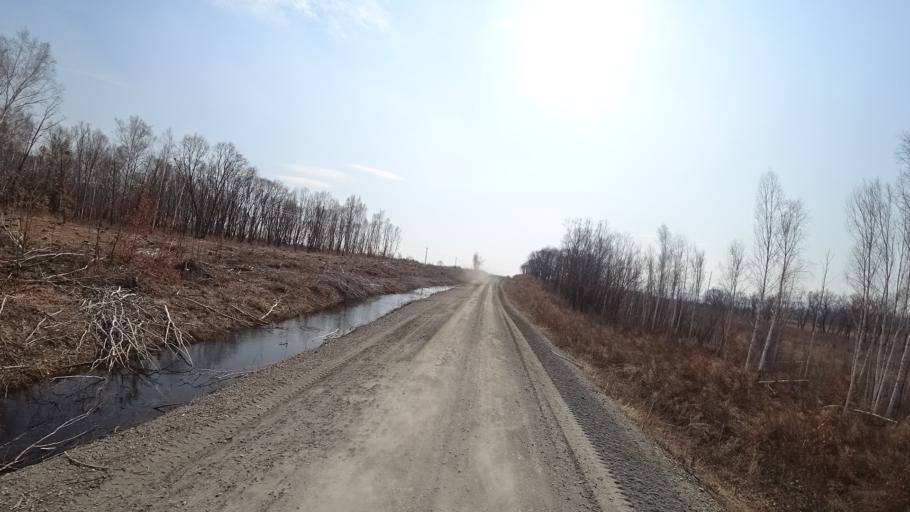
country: RU
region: Amur
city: Novobureyskiy
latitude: 49.8205
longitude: 129.9818
